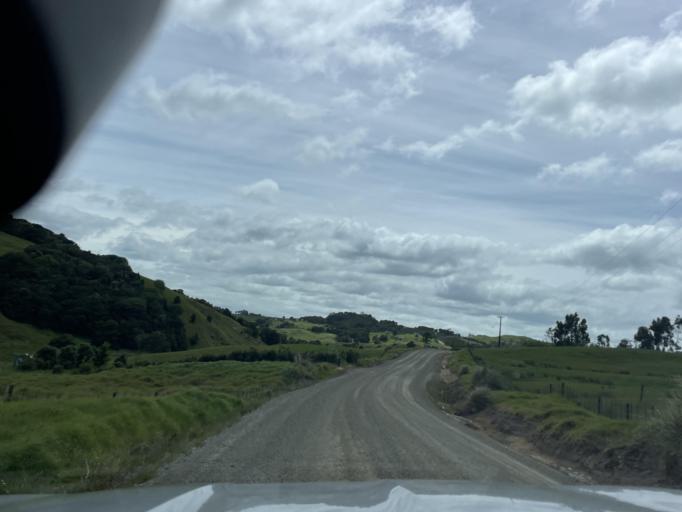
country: NZ
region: Auckland
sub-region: Auckland
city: Wellsford
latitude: -36.1644
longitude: 174.2830
